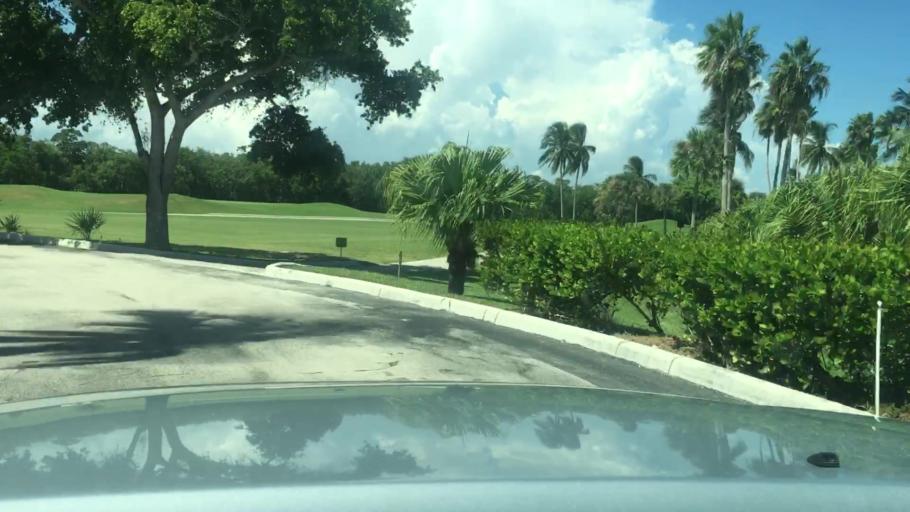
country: US
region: Florida
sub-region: Miami-Dade County
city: Key Biscayne
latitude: 25.7168
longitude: -80.1582
